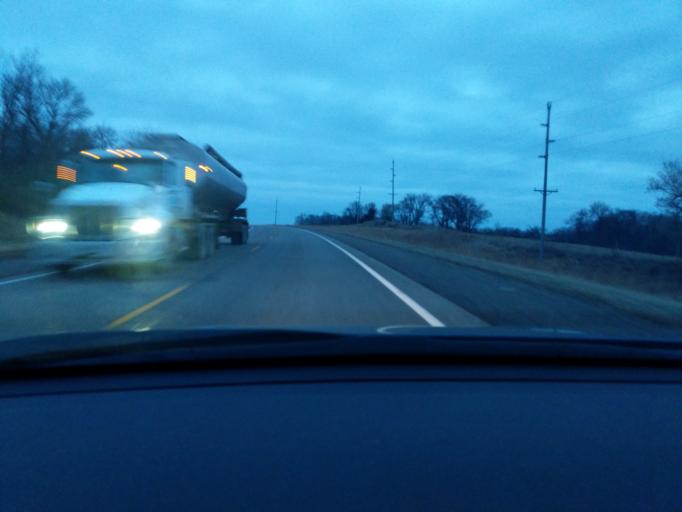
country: US
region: Minnesota
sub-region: Yellow Medicine County
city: Granite Falls
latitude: 44.7904
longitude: -95.4500
